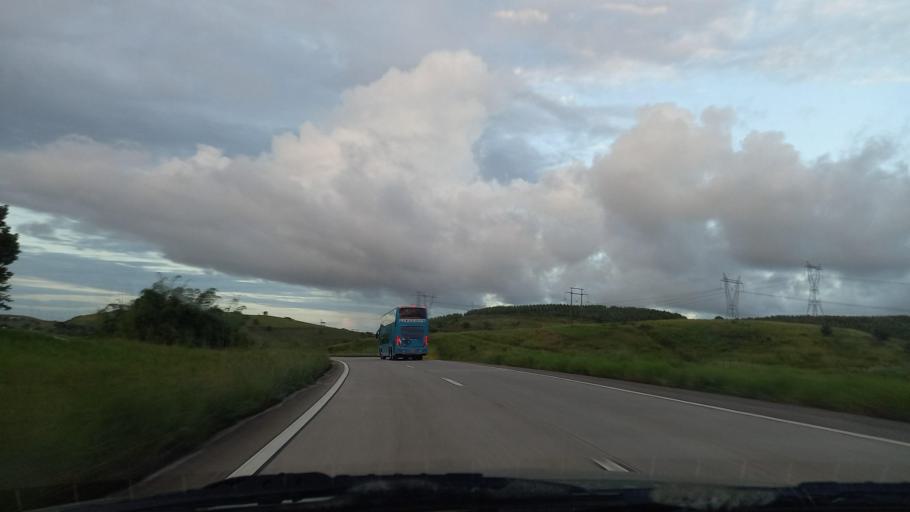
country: BR
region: Pernambuco
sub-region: Joaquim Nabuco
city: Joaquim Nabuco
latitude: -8.6032
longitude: -35.5337
